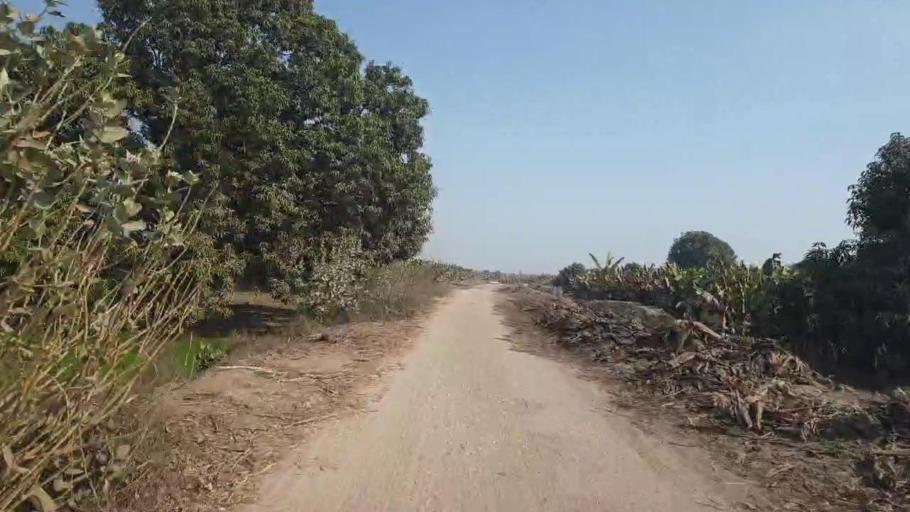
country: PK
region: Sindh
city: Tando Allahyar
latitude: 25.5641
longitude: 68.7529
